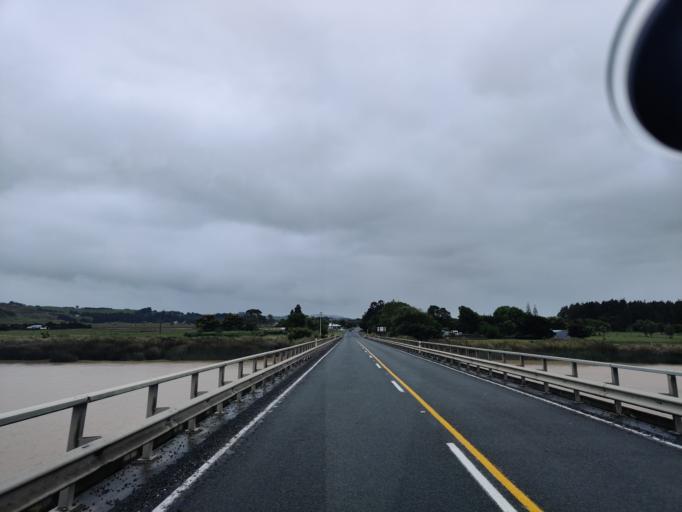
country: NZ
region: Northland
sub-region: Kaipara District
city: Dargaville
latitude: -35.9400
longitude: 173.8846
